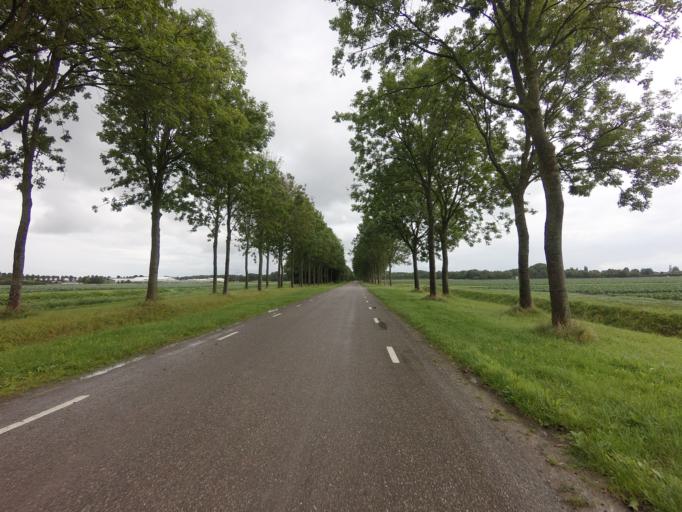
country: NL
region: North Holland
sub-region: Gemeente Enkhuizen
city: Enkhuizen
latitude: 52.7074
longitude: 5.2353
